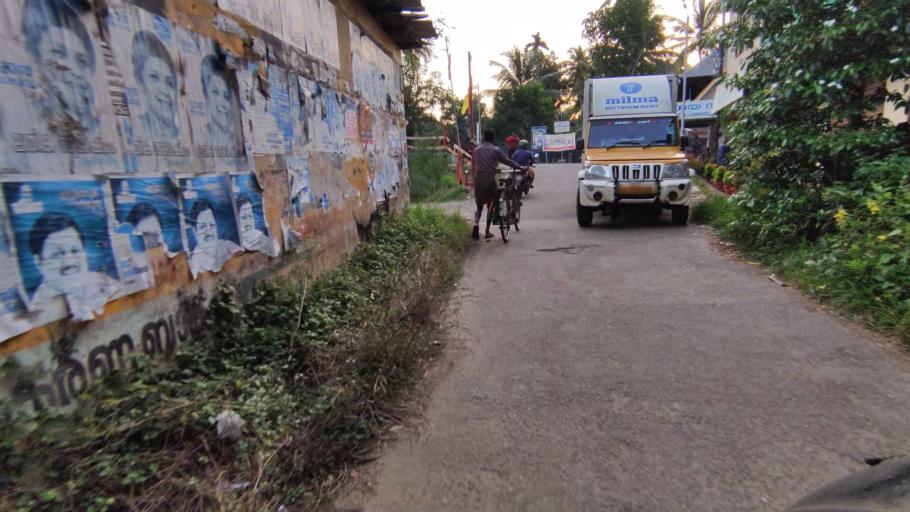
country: IN
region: Kerala
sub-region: Kottayam
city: Kottayam
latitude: 9.5769
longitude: 76.4354
